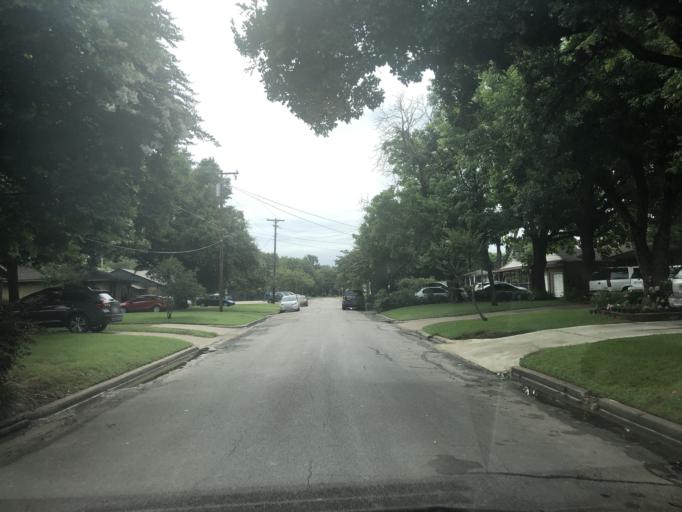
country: US
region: Texas
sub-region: Dallas County
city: Irving
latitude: 32.8074
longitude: -96.9458
